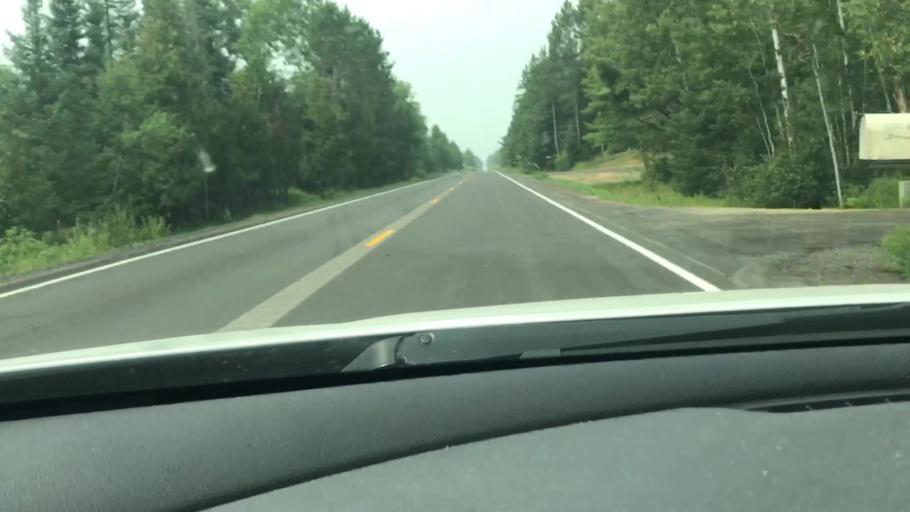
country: US
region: Minnesota
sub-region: Itasca County
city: Cohasset
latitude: 47.3496
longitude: -93.8359
